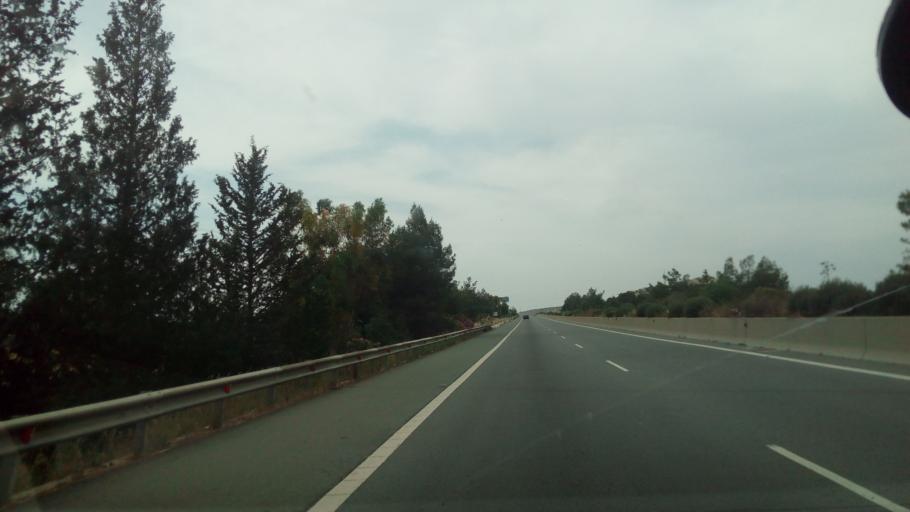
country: CY
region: Larnaka
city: Aradippou
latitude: 34.9678
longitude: 33.5541
